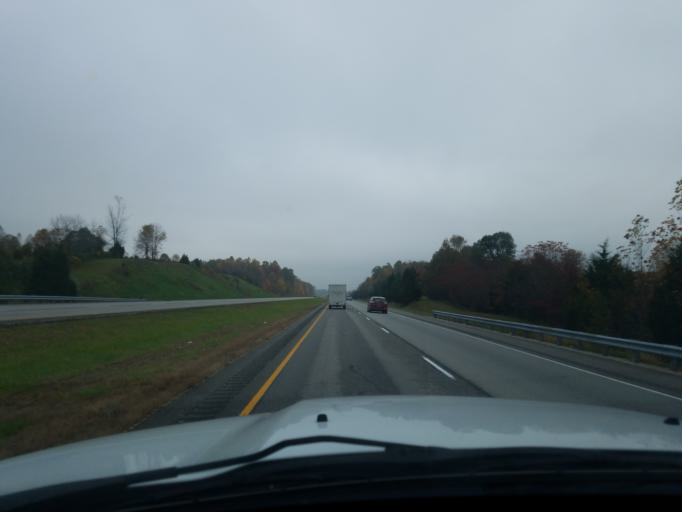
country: US
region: Kentucky
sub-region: Hardin County
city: Elizabethtown
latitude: 37.6335
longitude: -85.8270
